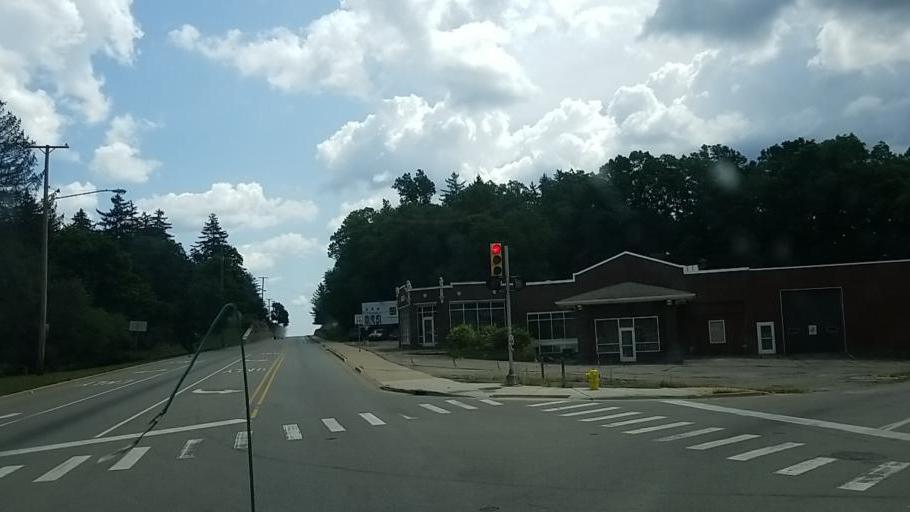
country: US
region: Michigan
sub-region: Kent County
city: Grand Rapids
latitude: 42.9859
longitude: -85.7076
